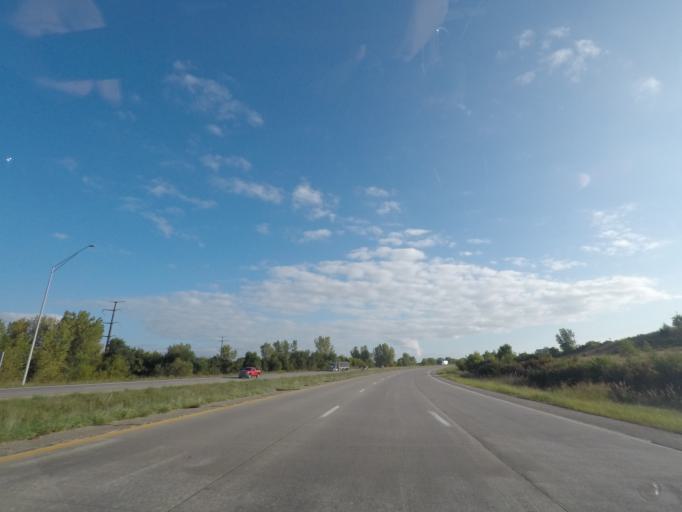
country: US
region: Iowa
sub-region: Polk County
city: Pleasant Hill
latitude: 41.5777
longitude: -93.5132
